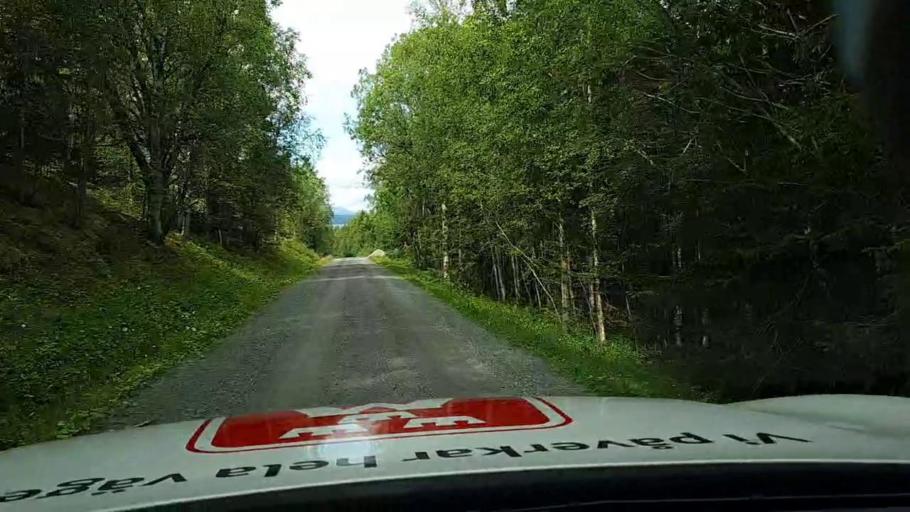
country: SE
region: Jaemtland
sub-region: Krokoms Kommun
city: Valla
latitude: 63.5924
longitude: 13.9998
